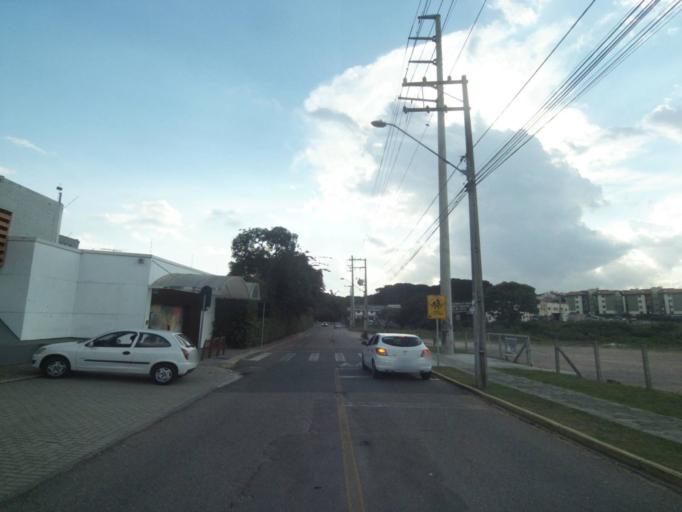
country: BR
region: Parana
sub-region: Sao Jose Dos Pinhais
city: Sao Jose dos Pinhais
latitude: -25.5354
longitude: -49.2830
